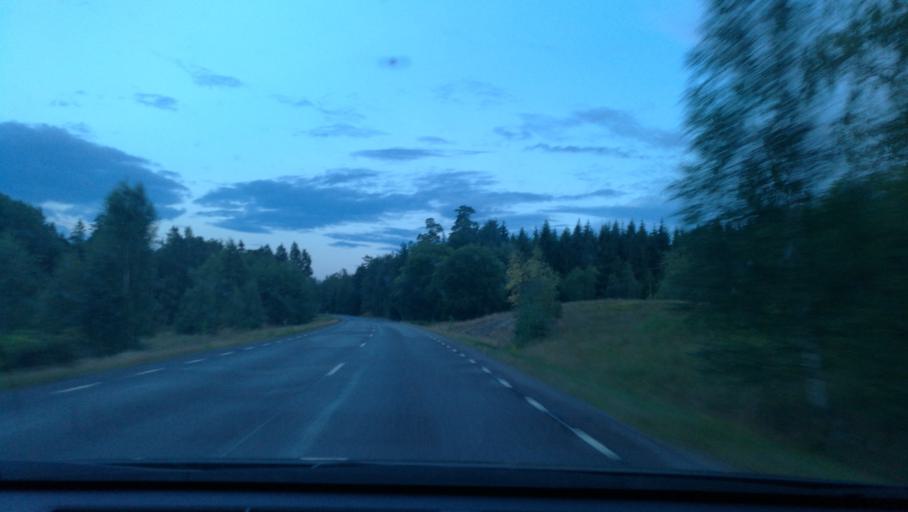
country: SE
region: OEstergoetland
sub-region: Norrkopings Kommun
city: Svartinge
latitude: 58.7748
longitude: 15.9670
